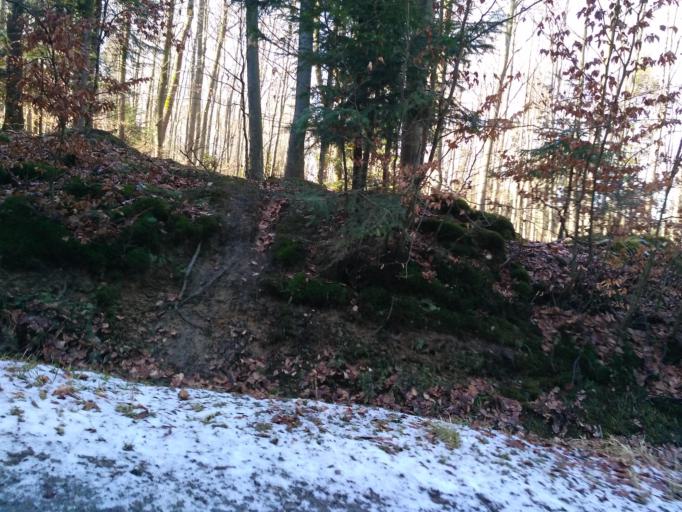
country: PL
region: Subcarpathian Voivodeship
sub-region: Powiat strzyzowski
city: Babica
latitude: 49.9544
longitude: 21.8677
